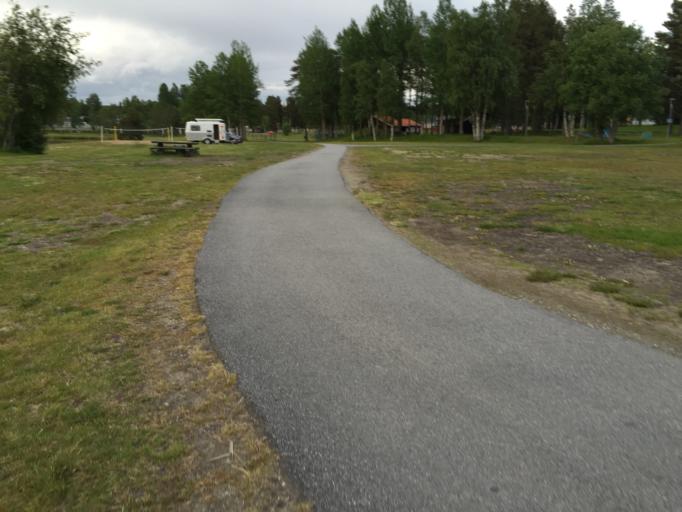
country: SE
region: Vaesterbotten
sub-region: Storumans Kommun
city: Storuman
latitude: 65.1003
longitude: 17.1149
